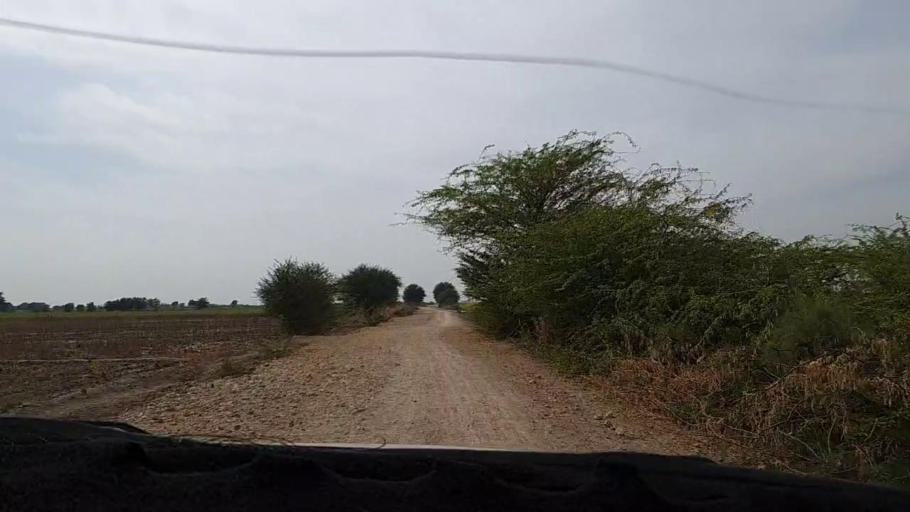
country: PK
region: Sindh
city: Pithoro
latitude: 25.5534
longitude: 69.3541
